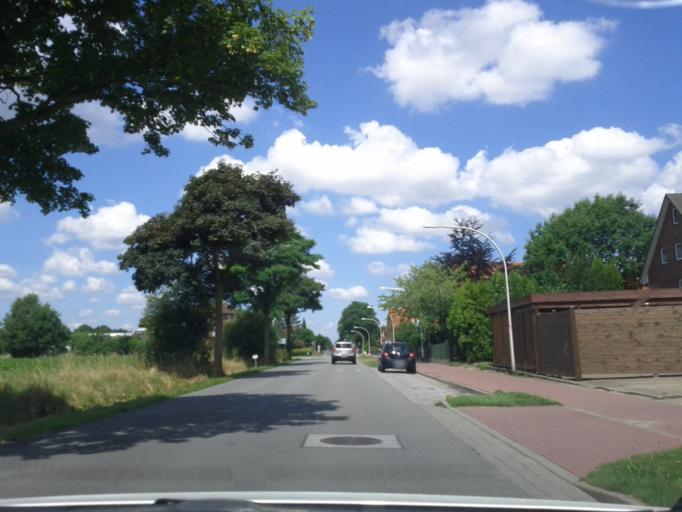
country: DE
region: Lower Saxony
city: Apensen
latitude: 53.4373
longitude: 9.6122
